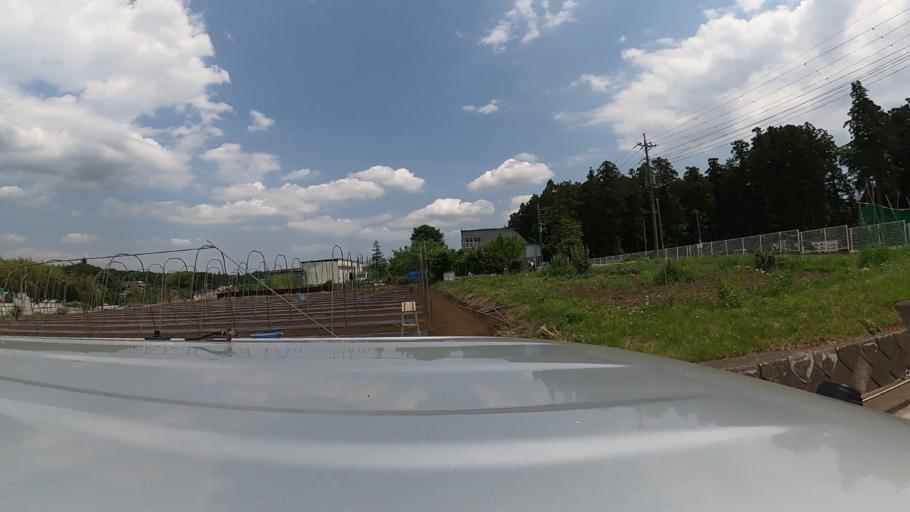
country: JP
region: Kanagawa
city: Chigasaki
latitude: 35.3930
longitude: 139.4209
